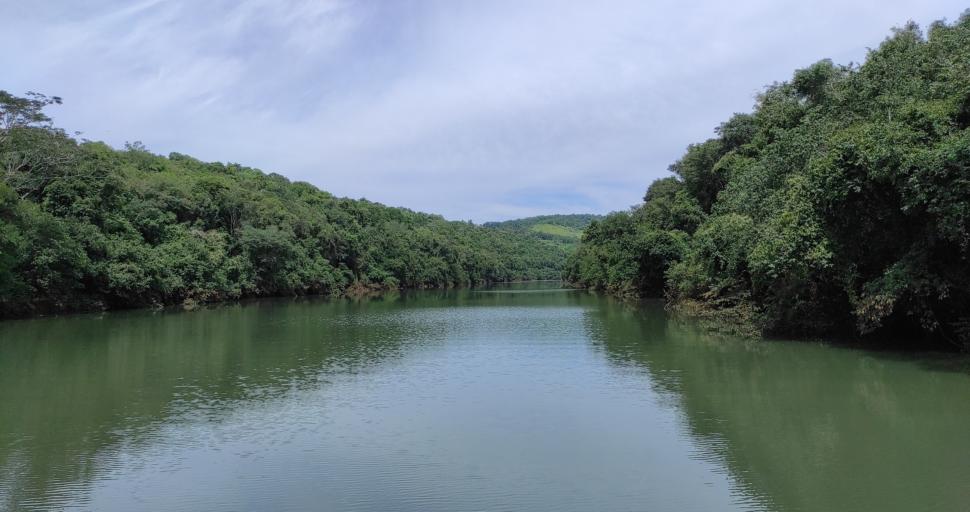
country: AR
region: Misiones
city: El Soberbio
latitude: -27.2812
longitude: -54.2002
